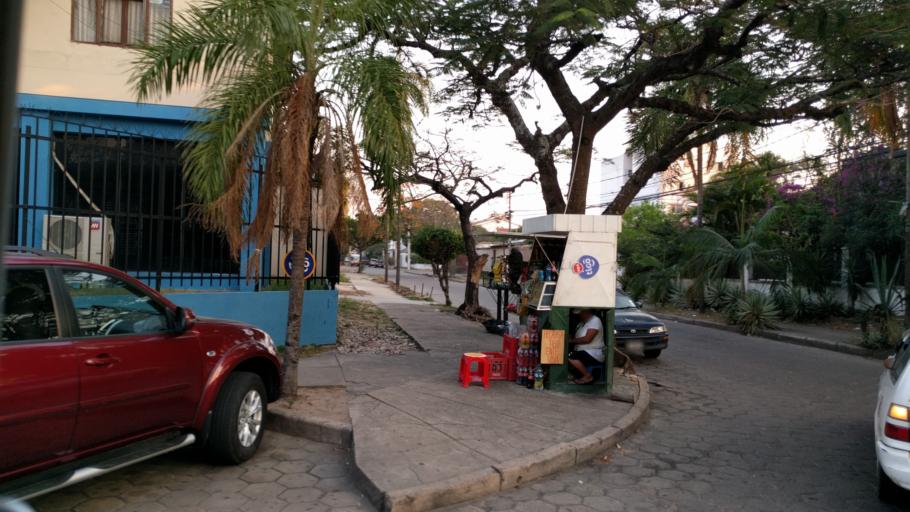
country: BO
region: Santa Cruz
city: Santa Cruz de la Sierra
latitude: -17.7813
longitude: -63.1899
